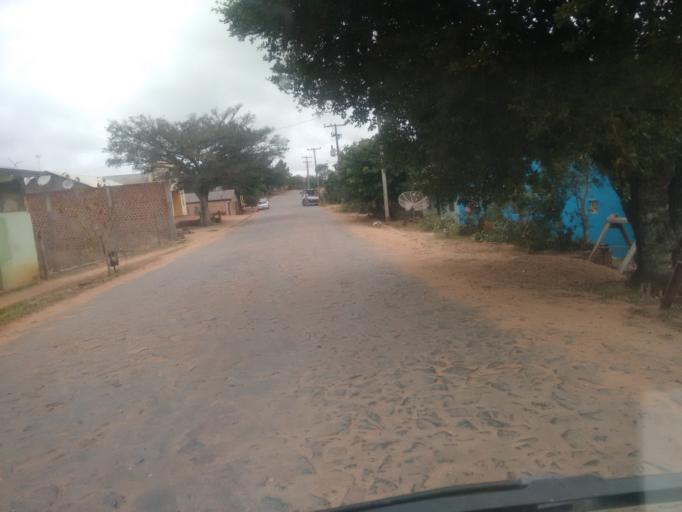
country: BR
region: Rio Grande do Sul
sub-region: Camaqua
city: Camaqua
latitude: -30.7920
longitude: -51.8312
